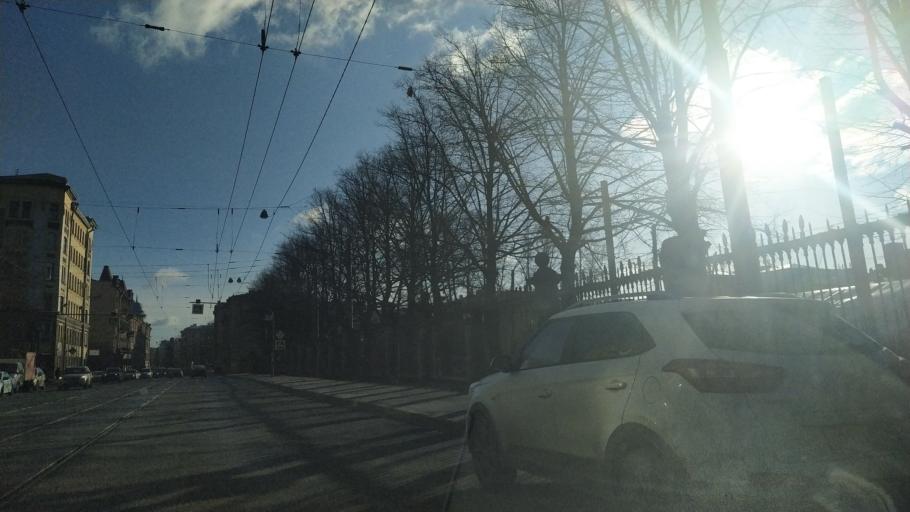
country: RU
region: Leningrad
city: Finlyandskiy
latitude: 59.9649
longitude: 30.3510
